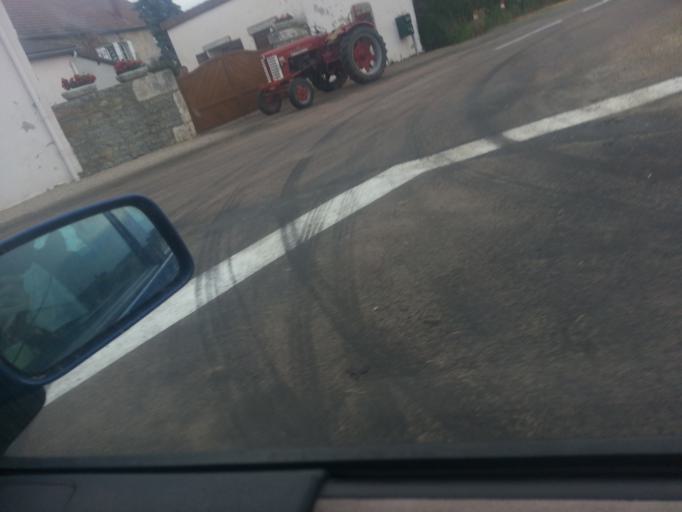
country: FR
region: Bourgogne
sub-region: Departement de Saone-et-Loire
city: Buxy
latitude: 46.7431
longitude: 4.6337
